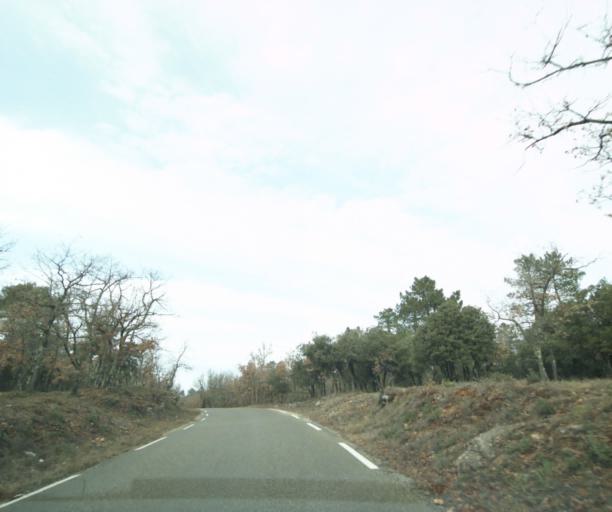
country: FR
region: Provence-Alpes-Cote d'Azur
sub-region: Departement du Var
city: Tourves
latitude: 43.3764
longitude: 5.8996
